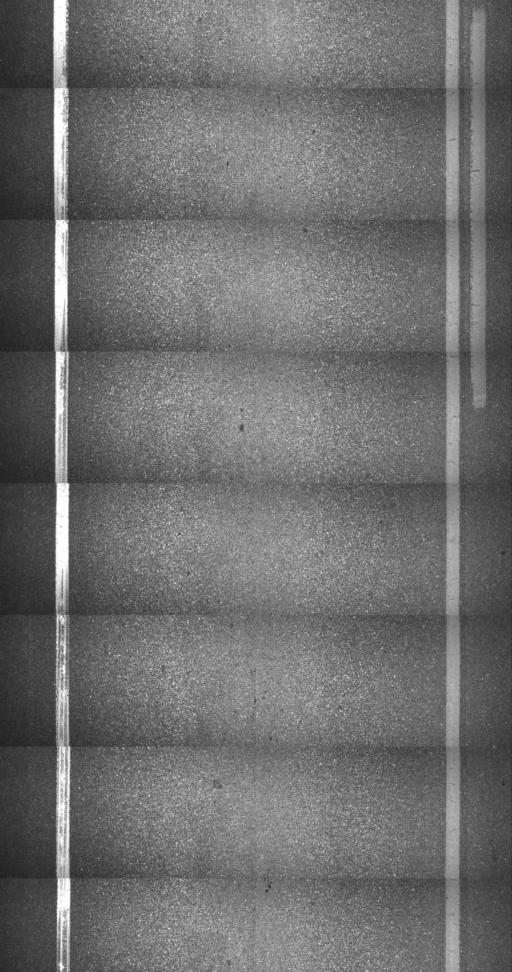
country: US
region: Vermont
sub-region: Addison County
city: Vergennes
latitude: 44.0929
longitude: -73.2323
